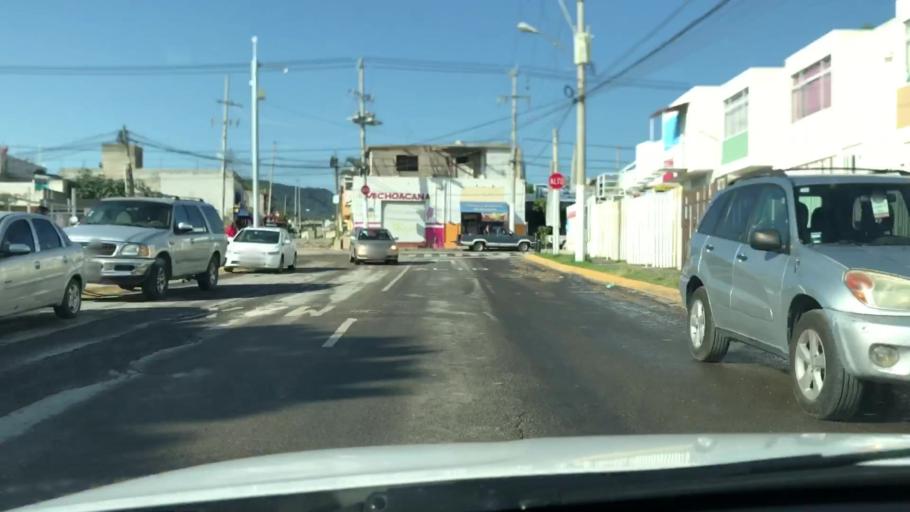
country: MX
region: Jalisco
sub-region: Tlajomulco de Zuniga
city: Palomar
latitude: 20.6268
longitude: -103.4786
